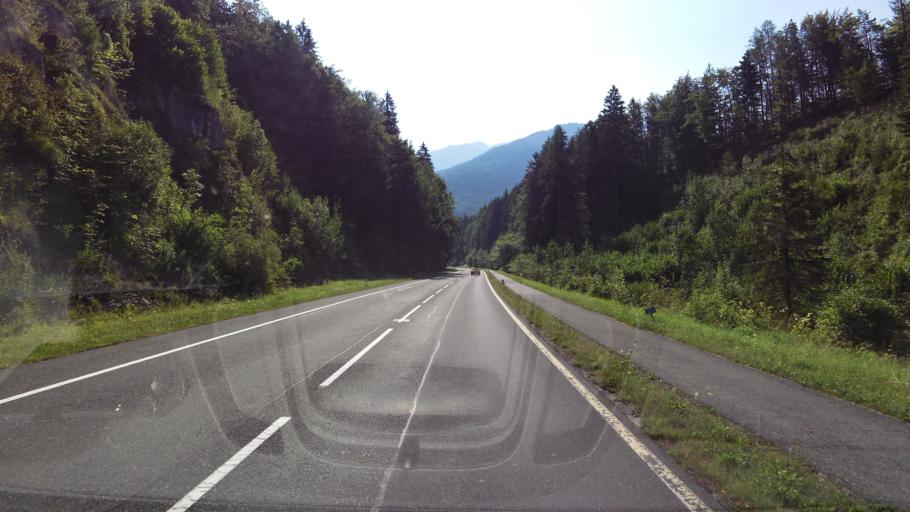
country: AT
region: Salzburg
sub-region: Politischer Bezirk Hallein
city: Golling an der Salzach
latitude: 47.5803
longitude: 13.1871
